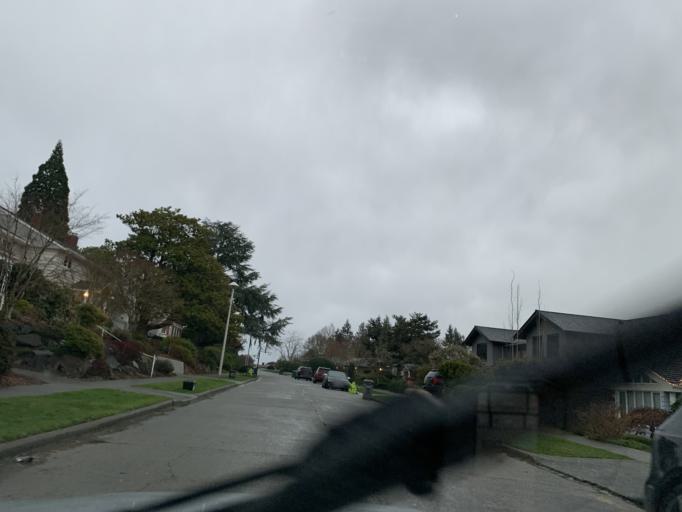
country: US
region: Washington
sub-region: King County
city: Yarrow Point
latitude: 47.6727
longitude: -122.2770
